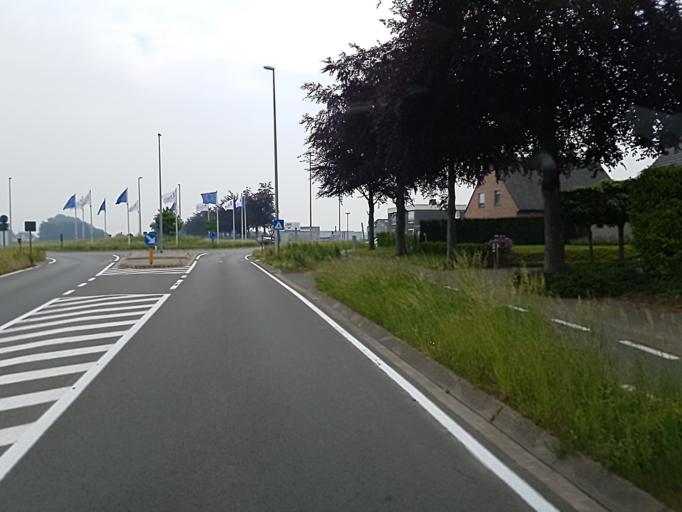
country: BE
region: Flanders
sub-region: Provincie West-Vlaanderen
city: Tielt
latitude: 50.9862
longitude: 3.3385
